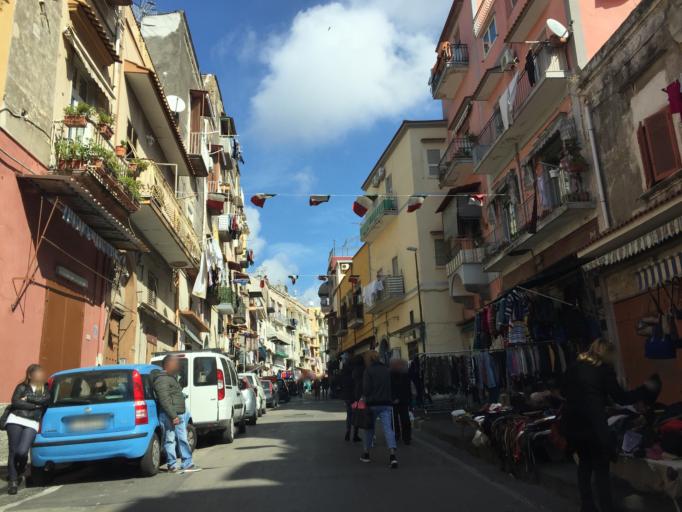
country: IT
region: Campania
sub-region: Provincia di Napoli
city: Ercolano
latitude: 40.8107
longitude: 14.3506
